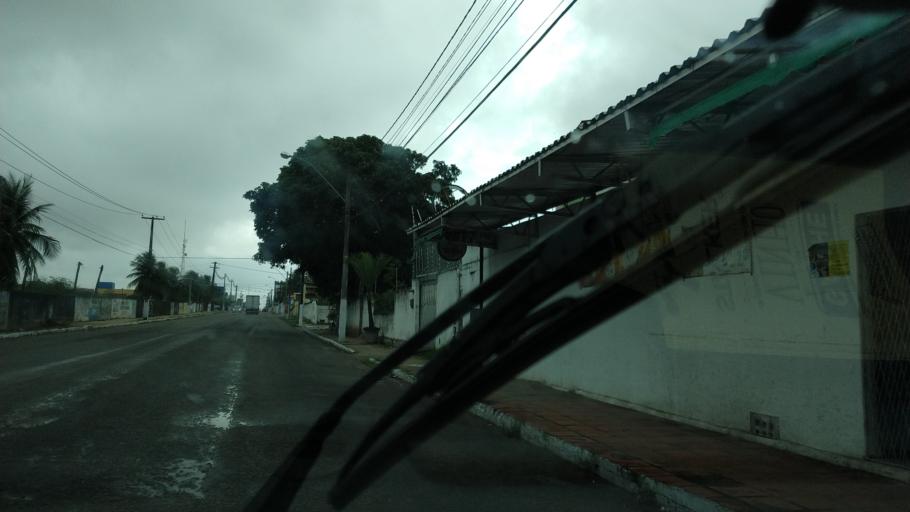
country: BR
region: Rio Grande do Norte
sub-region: Parnamirim
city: Parnamirim
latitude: -5.9249
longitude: -35.2706
